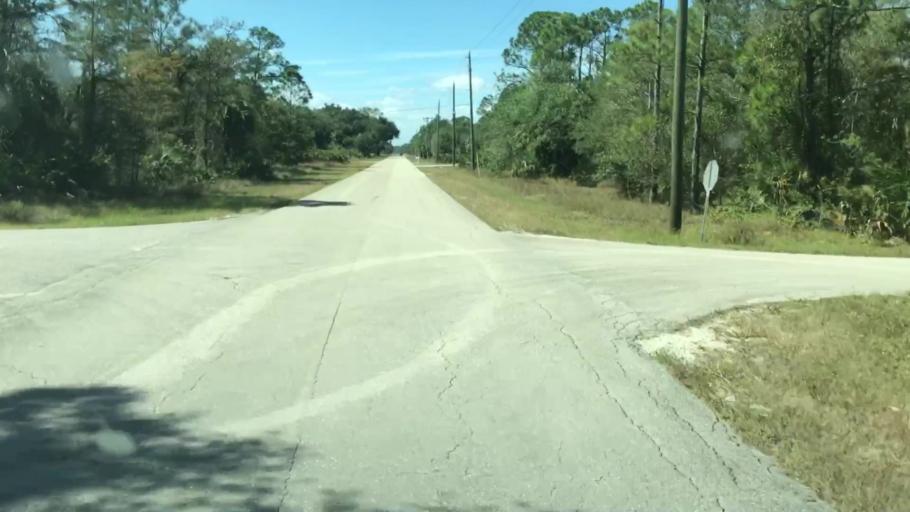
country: US
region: Florida
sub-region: Lee County
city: Lehigh Acres
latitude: 26.6619
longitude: -81.6212
